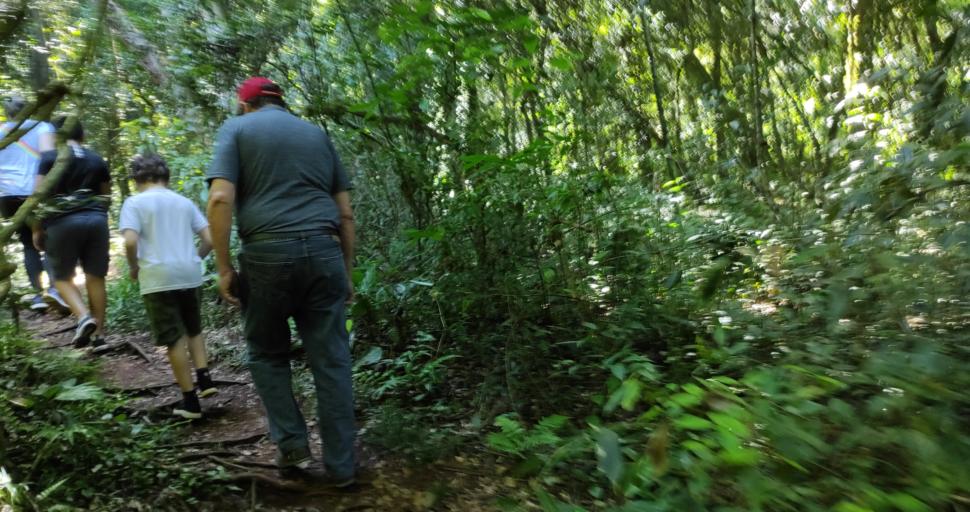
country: BR
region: Rio Grande do Sul
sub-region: Tres Passos
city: Tres Passos
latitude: -27.1508
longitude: -53.9007
